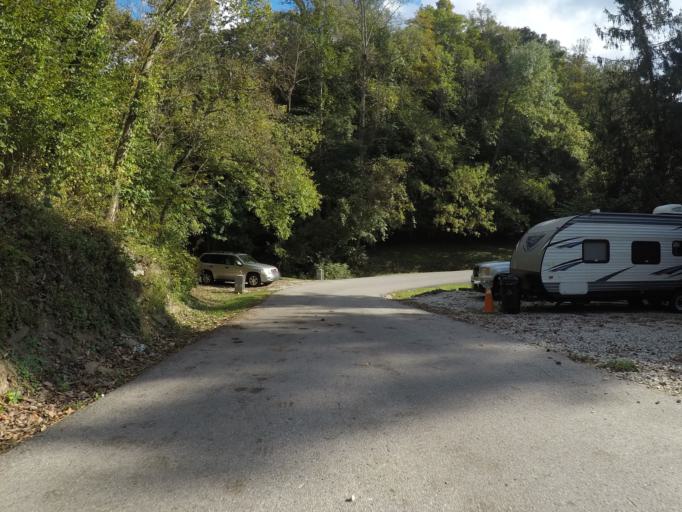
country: US
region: West Virginia
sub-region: Wayne County
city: Lavalette
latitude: 38.3605
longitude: -82.4847
